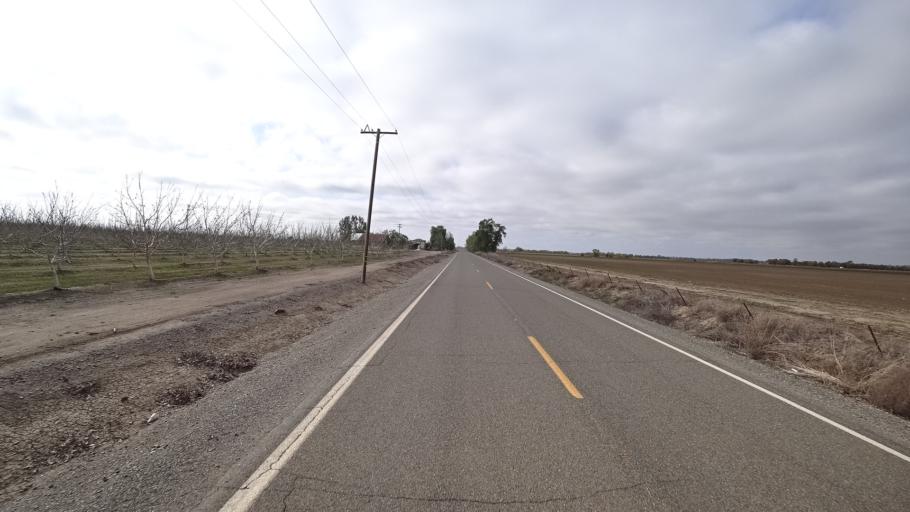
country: US
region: California
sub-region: Colusa County
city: Colusa
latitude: 39.4096
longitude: -121.9666
